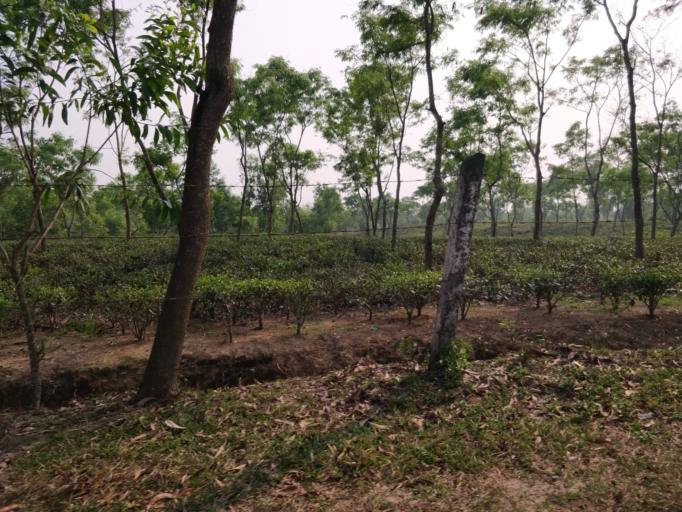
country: IN
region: Tripura
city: Khowai
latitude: 24.1303
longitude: 91.3867
